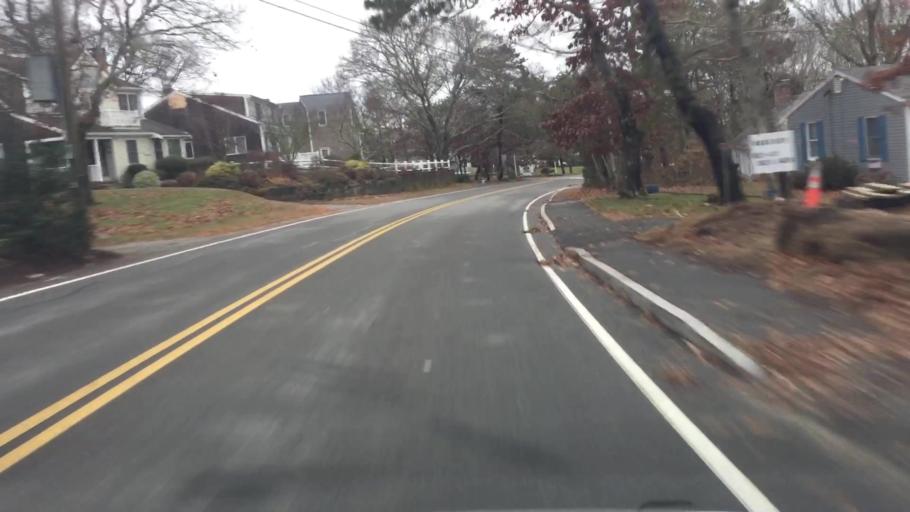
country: US
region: Massachusetts
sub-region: Barnstable County
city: West Falmouth
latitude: 41.6275
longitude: -70.6356
